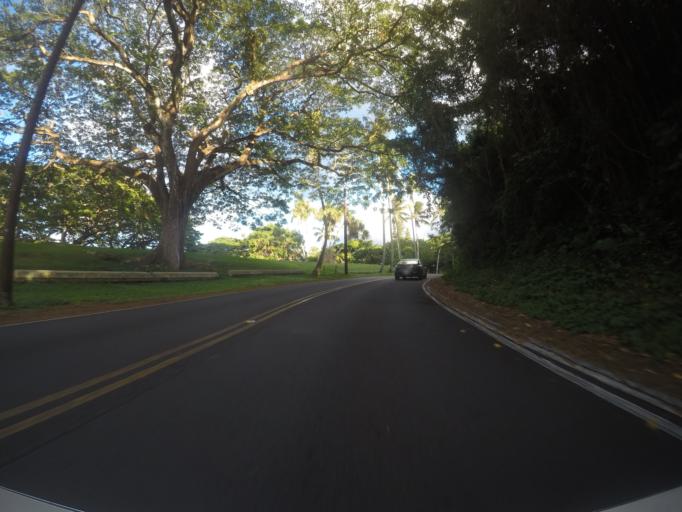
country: US
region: Hawaii
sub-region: Honolulu County
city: He'eia
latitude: 21.4413
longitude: -157.8102
